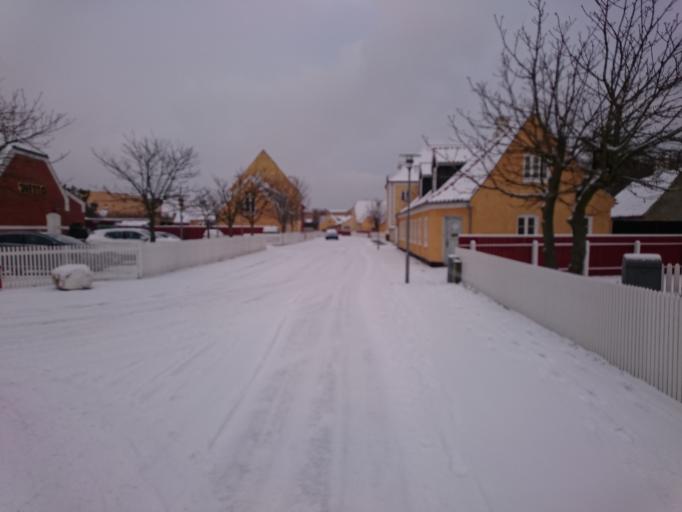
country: DK
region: North Denmark
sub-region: Frederikshavn Kommune
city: Skagen
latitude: 57.7186
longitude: 10.5811
